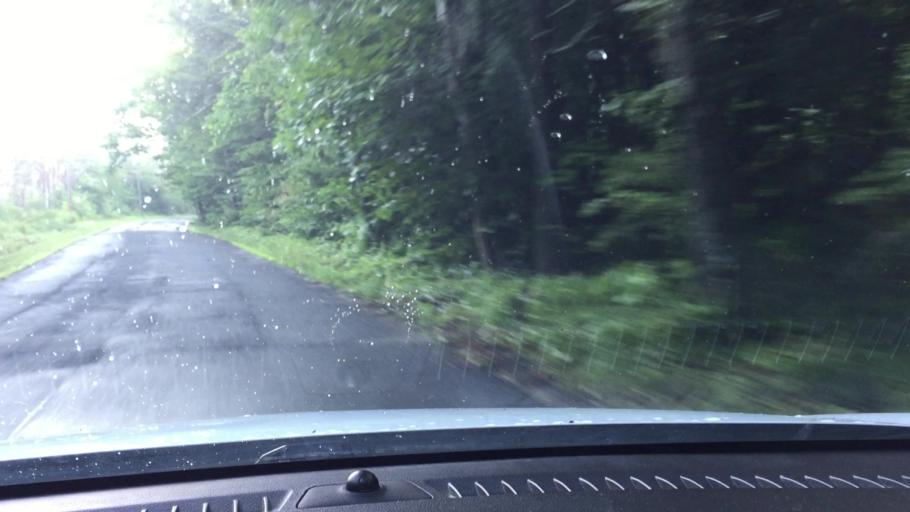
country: US
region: Massachusetts
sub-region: Berkshire County
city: Becket
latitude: 42.3868
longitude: -72.9776
